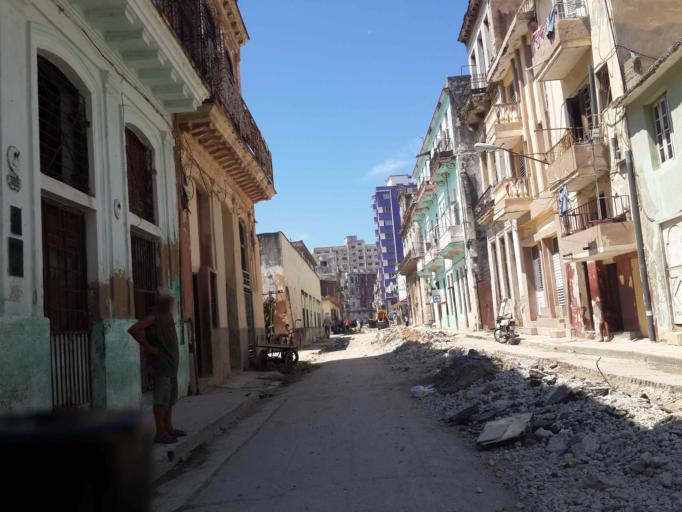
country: CU
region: La Habana
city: Centro Habana
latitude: 23.1410
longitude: -82.3622
